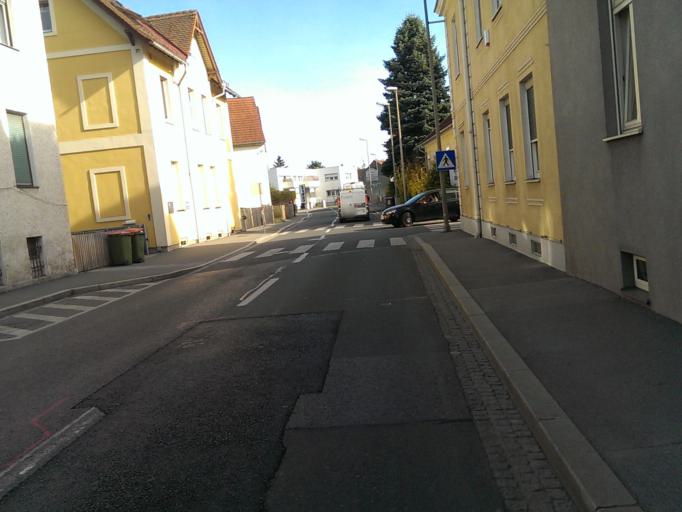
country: AT
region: Styria
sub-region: Graz Stadt
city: Graz
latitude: 47.0465
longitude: 15.4523
